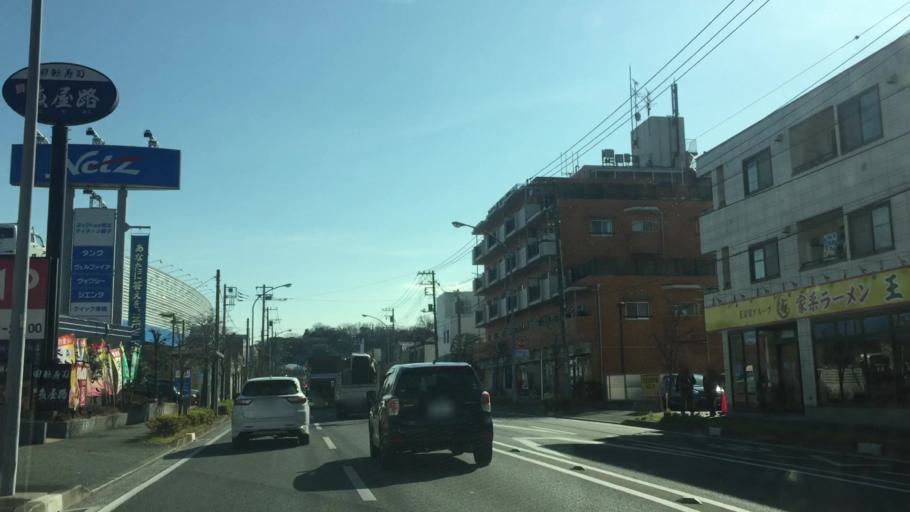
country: JP
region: Kanagawa
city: Yokohama
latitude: 35.3714
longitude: 139.6121
